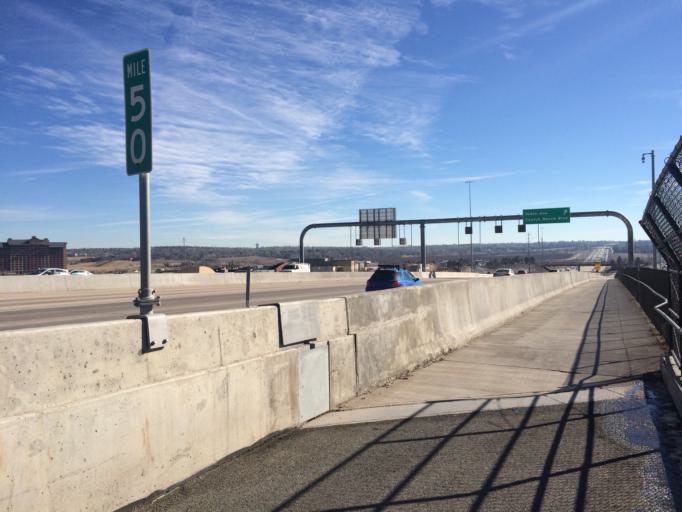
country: US
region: Colorado
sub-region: Broomfield County
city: Broomfield
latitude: 39.8915
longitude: -105.0755
